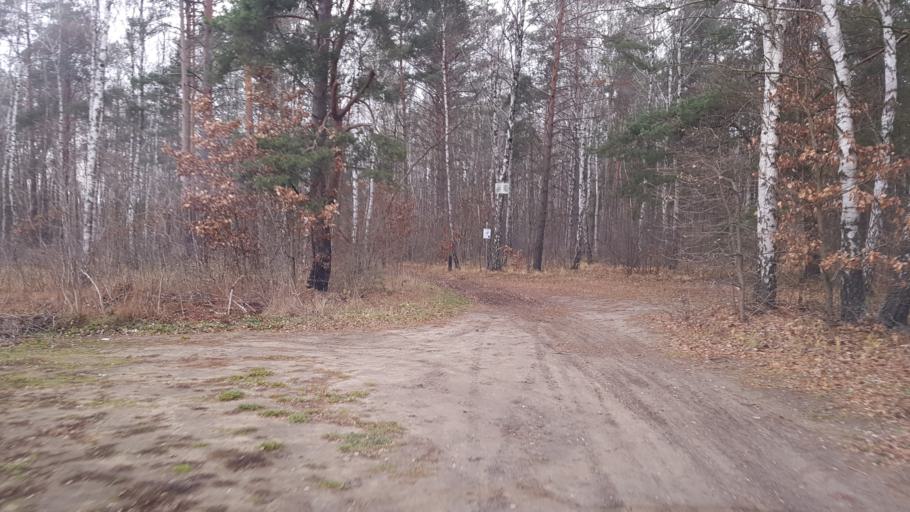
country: DE
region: Brandenburg
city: Sallgast
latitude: 51.5760
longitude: 13.8473
